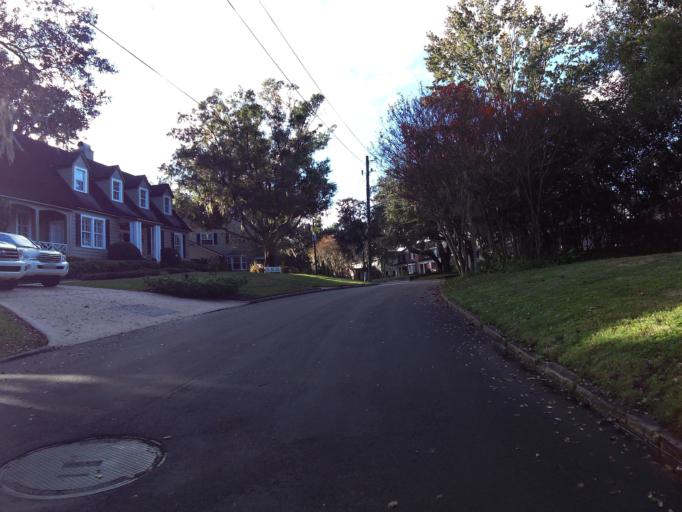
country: US
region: Florida
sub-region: Duval County
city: Jacksonville
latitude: 30.2945
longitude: -81.6518
